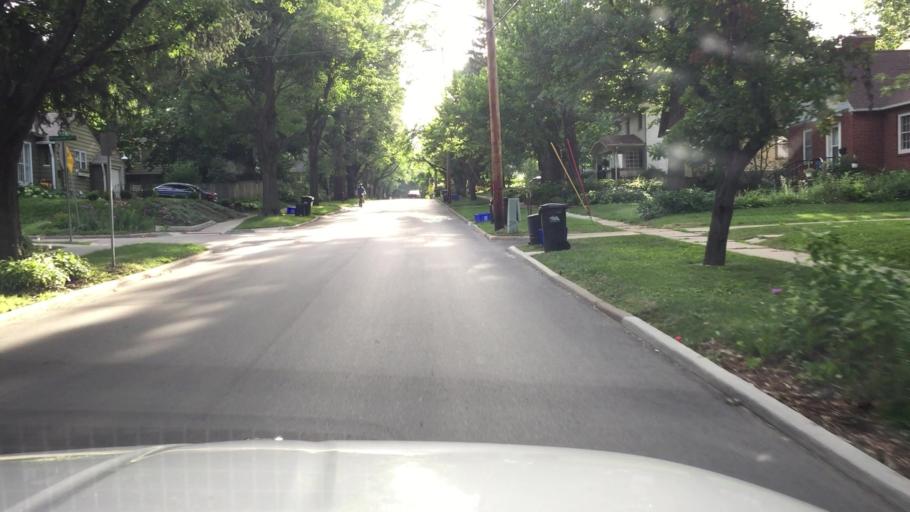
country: US
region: Iowa
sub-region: Johnson County
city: Iowa City
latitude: 41.6523
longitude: -91.5169
